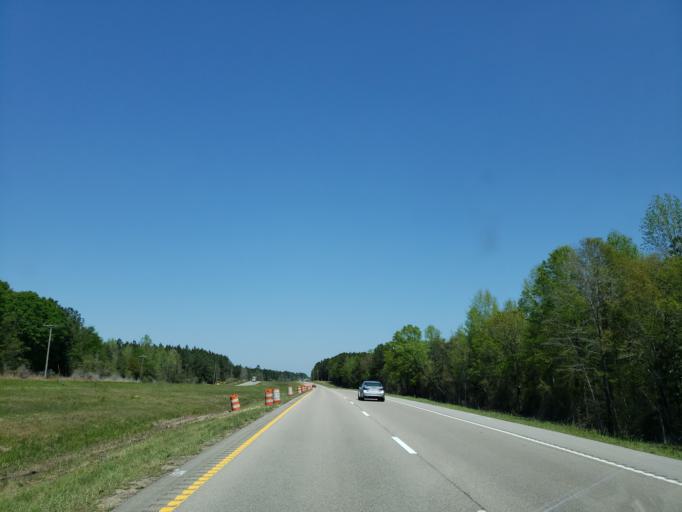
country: US
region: Mississippi
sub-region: Stone County
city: Wiggins
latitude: 31.0011
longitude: -89.2012
